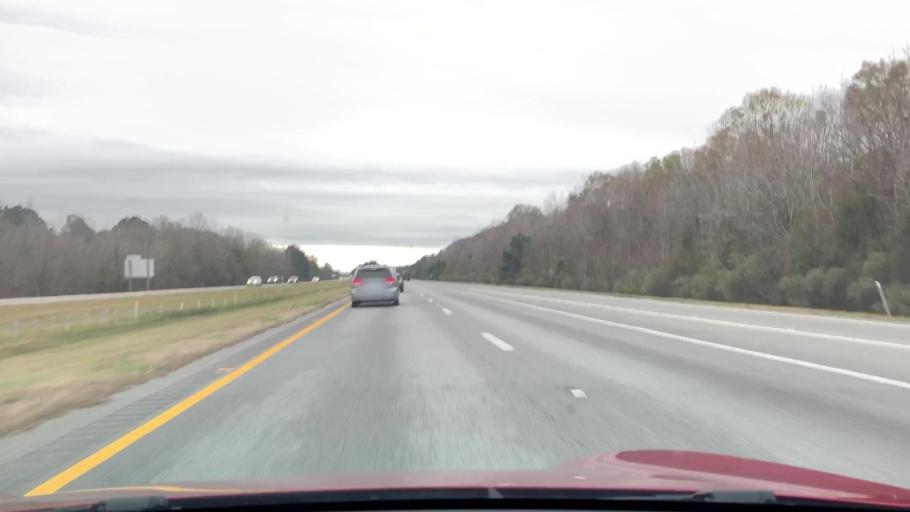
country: US
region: South Carolina
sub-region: Orangeburg County
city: Holly Hill
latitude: 33.3783
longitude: -80.5207
